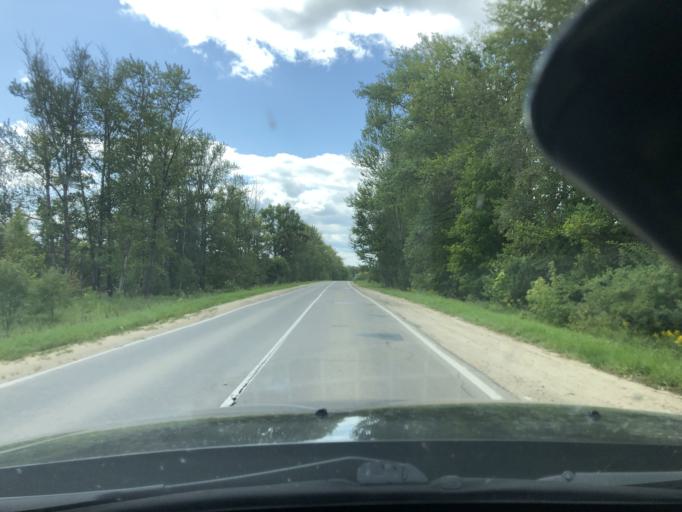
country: RU
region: Tula
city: Revyakino
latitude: 54.3497
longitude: 37.6235
